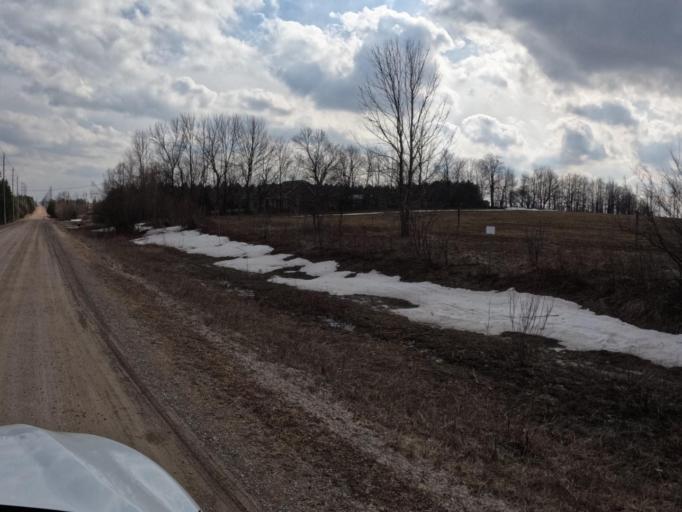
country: CA
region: Ontario
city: Shelburne
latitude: 43.9743
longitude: -80.3022
